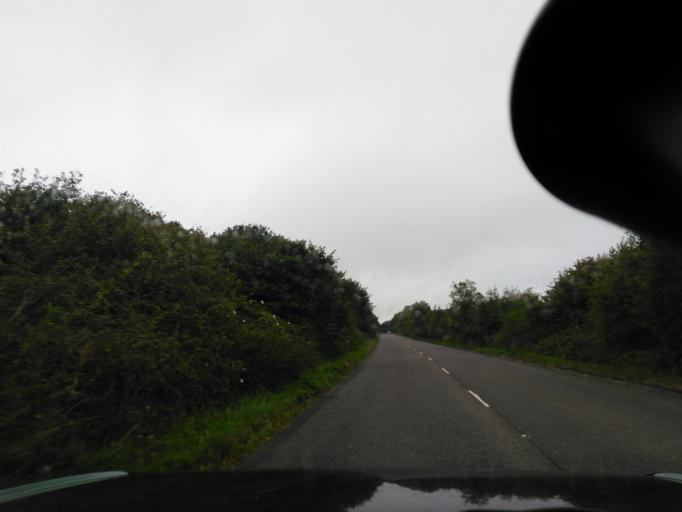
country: GB
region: England
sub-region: Wiltshire
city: Chicklade
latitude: 51.1014
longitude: -2.1631
